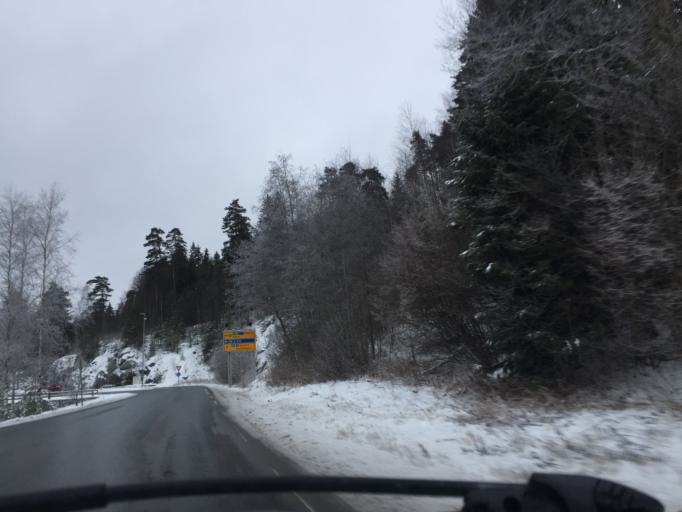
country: NO
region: Akershus
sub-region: As
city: As
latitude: 59.7059
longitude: 10.7398
